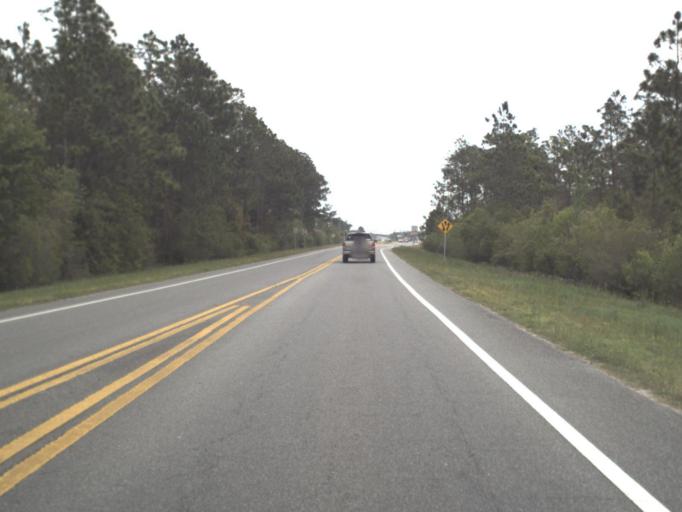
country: US
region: Florida
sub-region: Escambia County
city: Myrtle Grove
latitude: 30.4035
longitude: -87.3486
